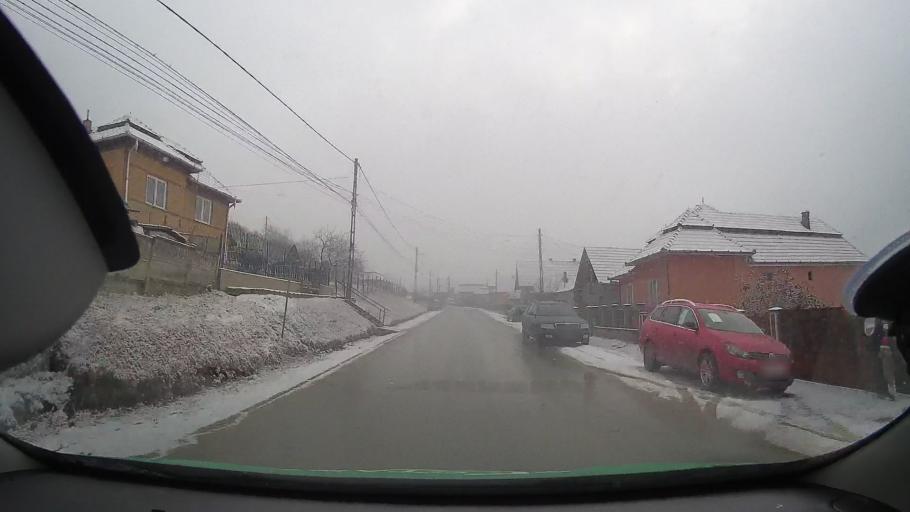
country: RO
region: Alba
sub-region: Comuna Lopadea Noua
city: Lopadea Noua
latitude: 46.2955
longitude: 23.8151
